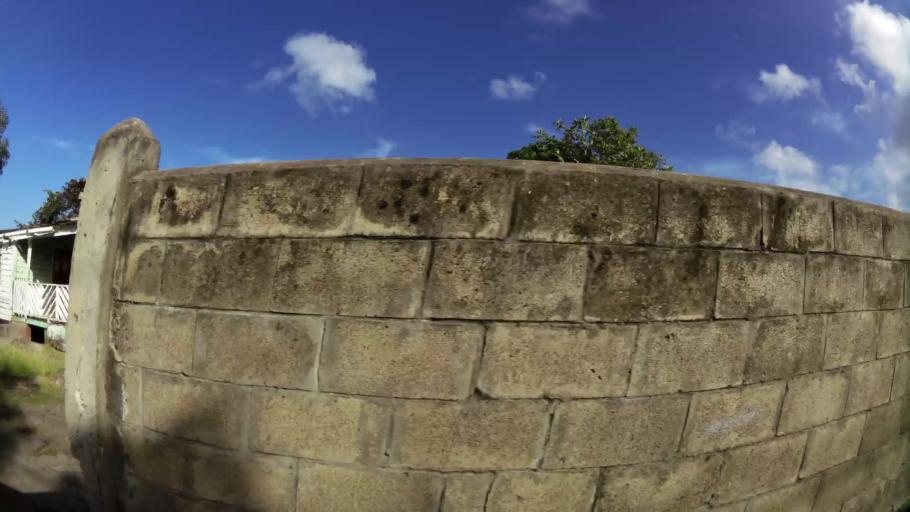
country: KN
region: Saint Paul Charlestown
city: Charlestown
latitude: 17.1433
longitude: -62.6251
